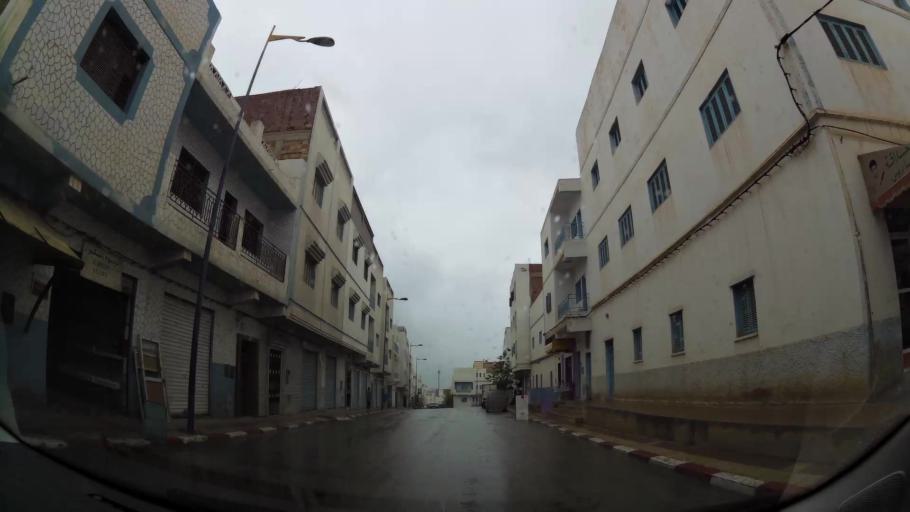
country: MA
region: Taza-Al Hoceima-Taounate
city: Imzourene
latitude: 35.1513
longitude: -3.8490
